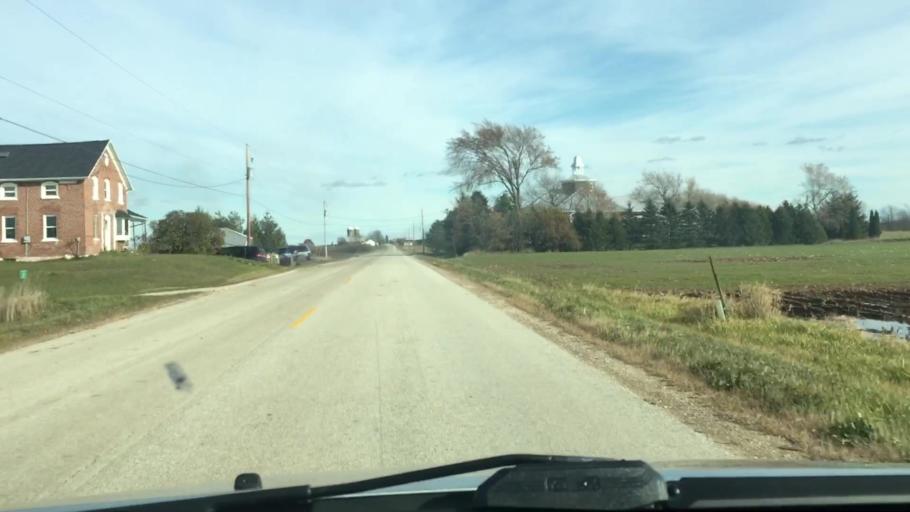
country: US
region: Wisconsin
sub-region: Kewaunee County
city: Luxemburg
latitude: 44.6976
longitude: -87.6118
